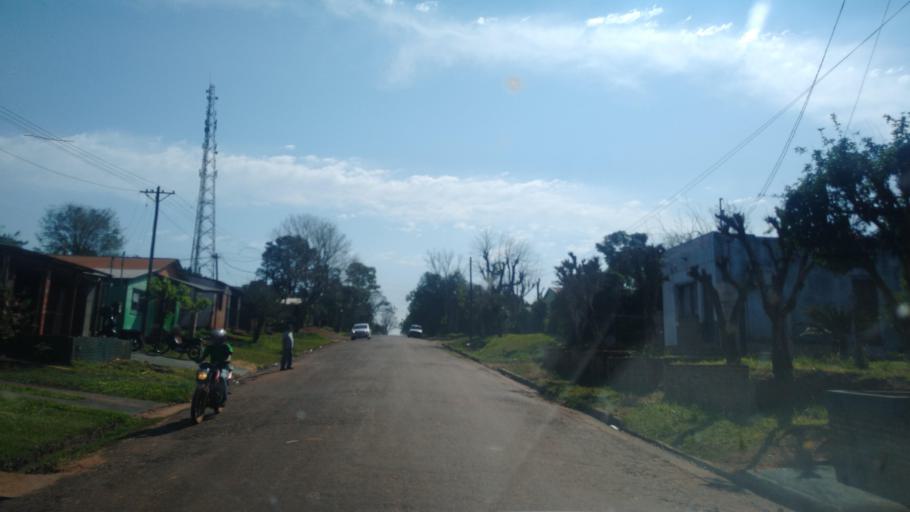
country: AR
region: Misiones
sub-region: Departamento de San Ignacio
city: San Ignacio
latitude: -27.2636
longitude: -55.5411
